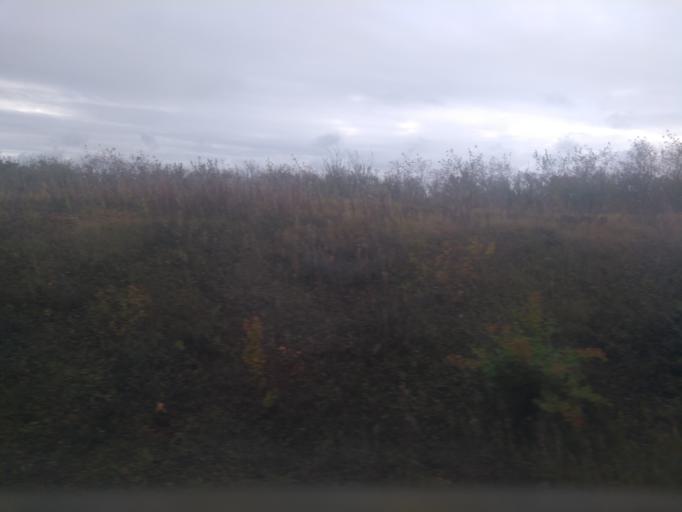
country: RU
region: Udmurtiya
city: Alnashi
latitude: 56.2180
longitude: 52.6424
